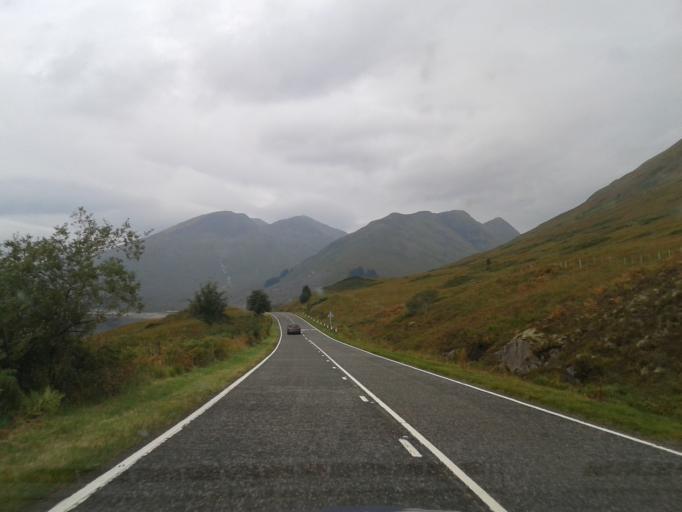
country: GB
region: Scotland
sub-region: Highland
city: Fort William
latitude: 57.1544
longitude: -5.1368
